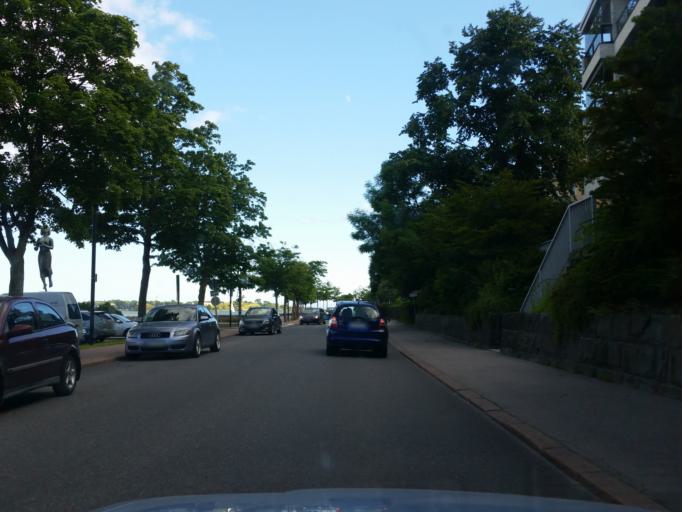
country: FI
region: Uusimaa
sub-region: Helsinki
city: Helsinki
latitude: 60.1592
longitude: 24.9613
